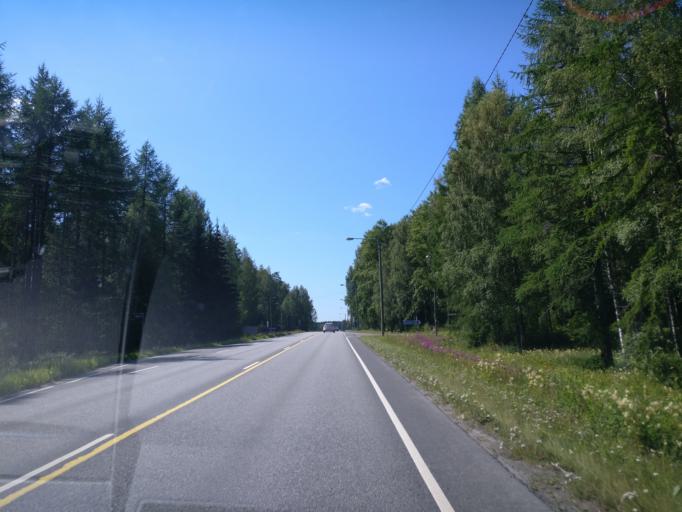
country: FI
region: Satakunta
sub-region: Pori
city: Kullaa
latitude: 61.4636
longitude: 22.1585
